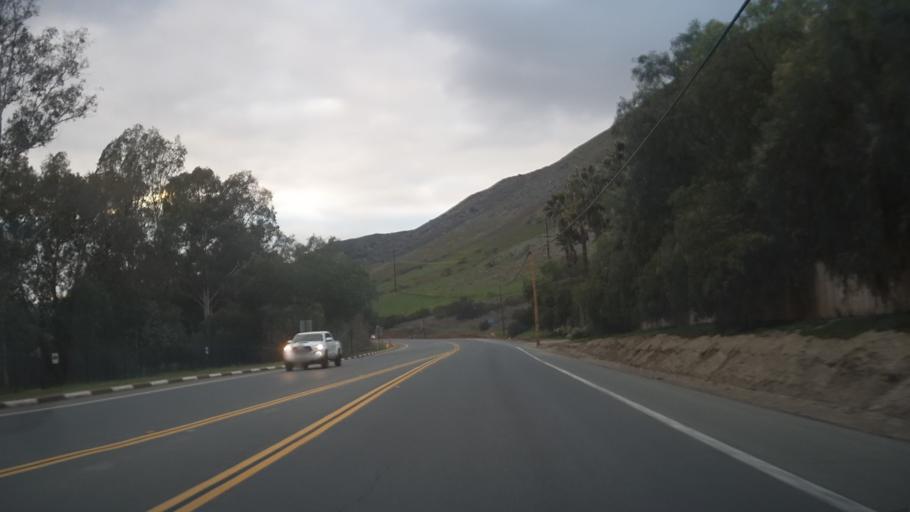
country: US
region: California
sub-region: San Diego County
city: Crest
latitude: 32.7817
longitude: -116.8531
